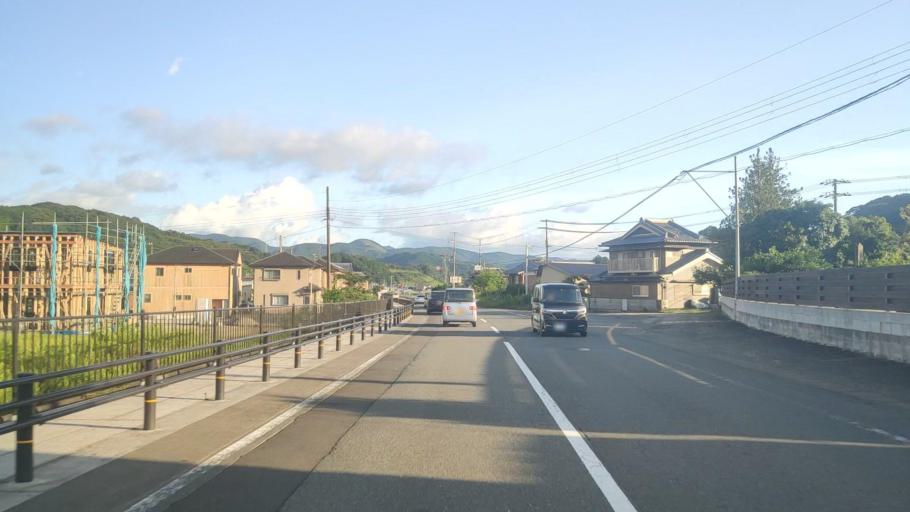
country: JP
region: Wakayama
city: Tanabe
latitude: 33.7205
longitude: 135.4456
